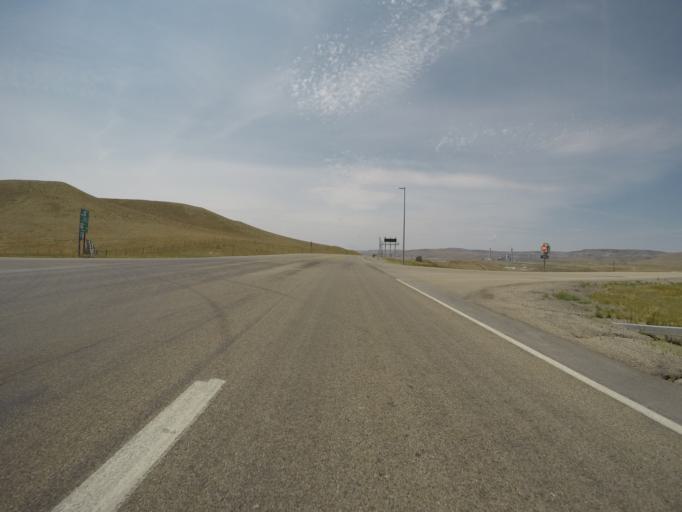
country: US
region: Wyoming
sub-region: Lincoln County
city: Kemmerer
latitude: 41.7708
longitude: -110.5538
